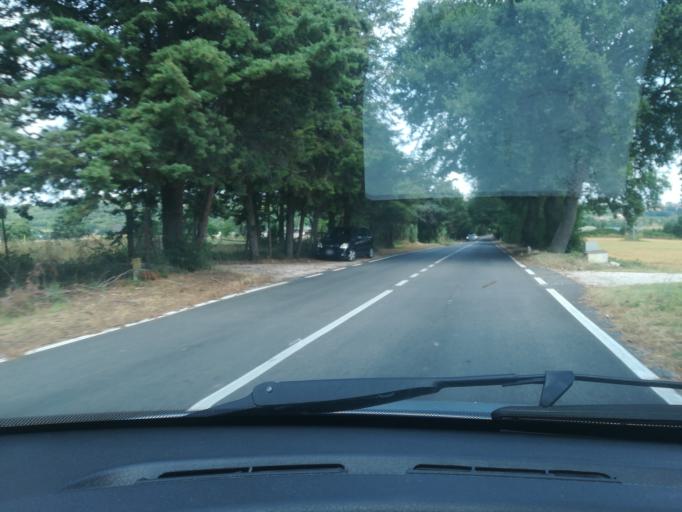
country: IT
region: The Marches
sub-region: Provincia di Macerata
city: Sforzacosta
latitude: 43.2704
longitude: 13.4370
